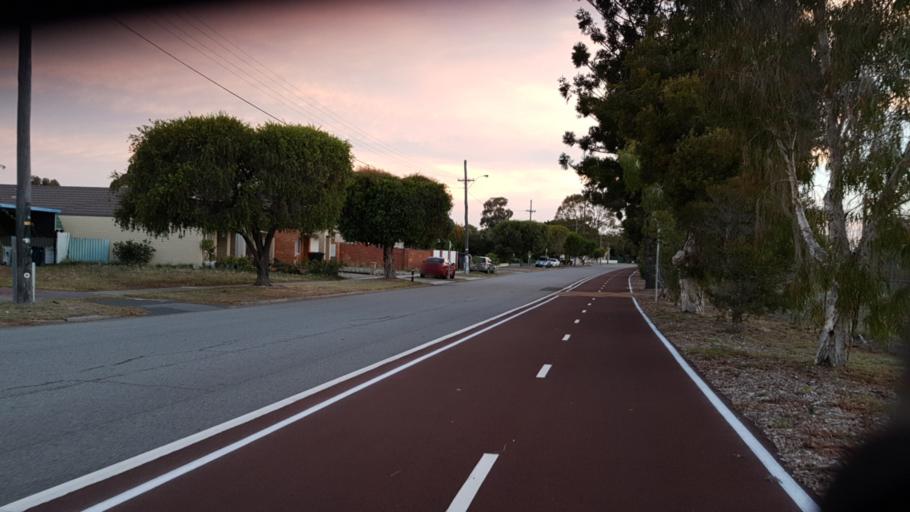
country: AU
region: Western Australia
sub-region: Victoria Park
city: East Victoria Park
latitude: -31.9838
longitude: 115.9142
